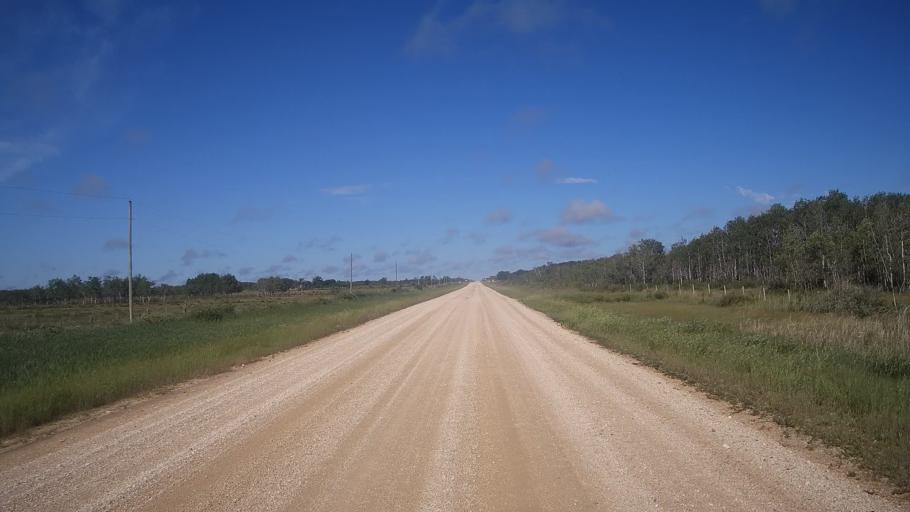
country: CA
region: Manitoba
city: Stonewall
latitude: 50.2411
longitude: -97.7252
